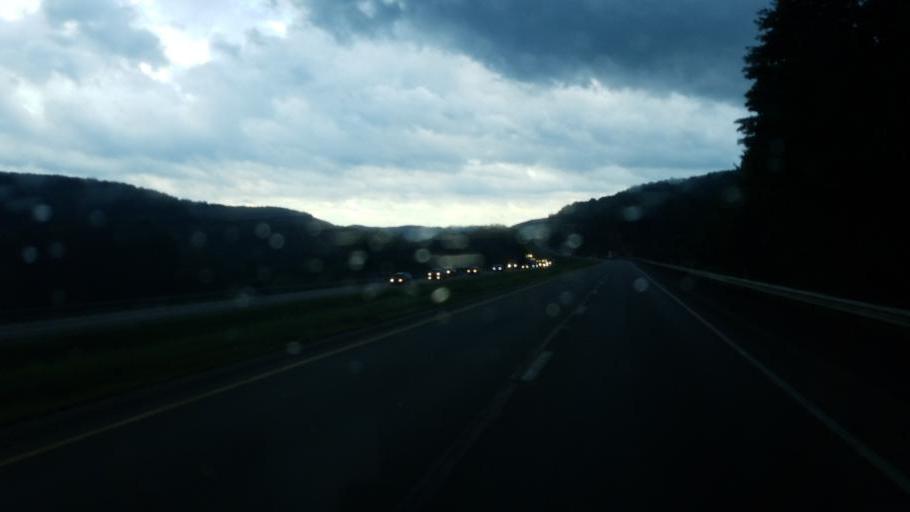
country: US
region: Pennsylvania
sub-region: Butler County
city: Prospect
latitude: 40.8780
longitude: -80.1143
